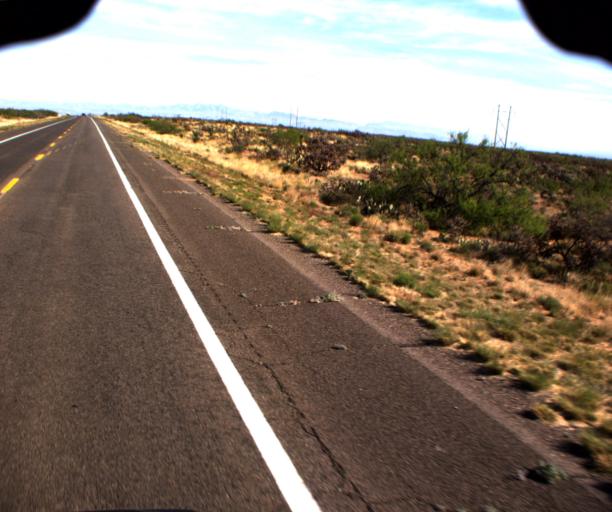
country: US
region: Arizona
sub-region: Graham County
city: Swift Trail Junction
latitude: 32.6214
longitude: -109.6891
